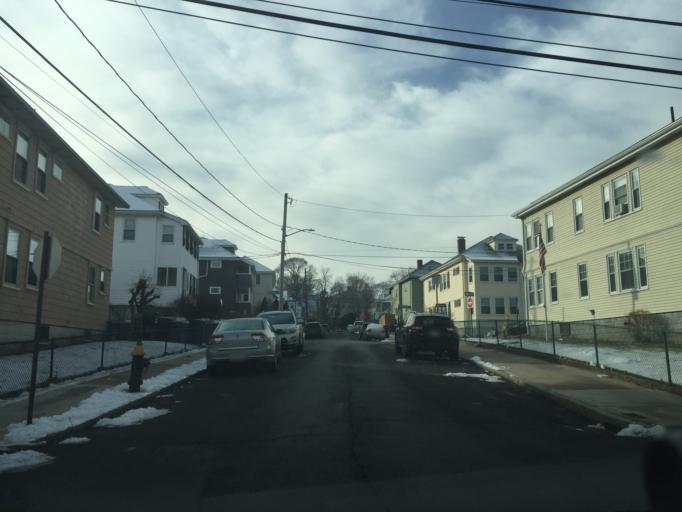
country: US
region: Massachusetts
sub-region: Norfolk County
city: Brookline
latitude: 42.3538
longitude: -71.1487
